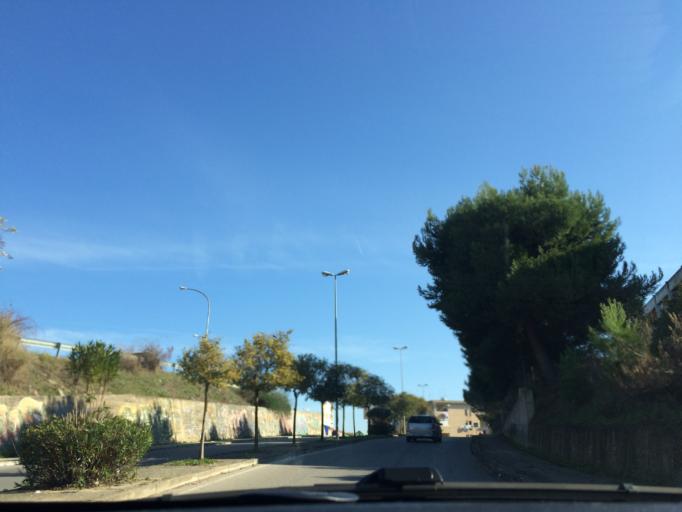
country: IT
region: Basilicate
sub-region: Provincia di Matera
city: Matera
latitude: 40.6838
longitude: 16.5829
